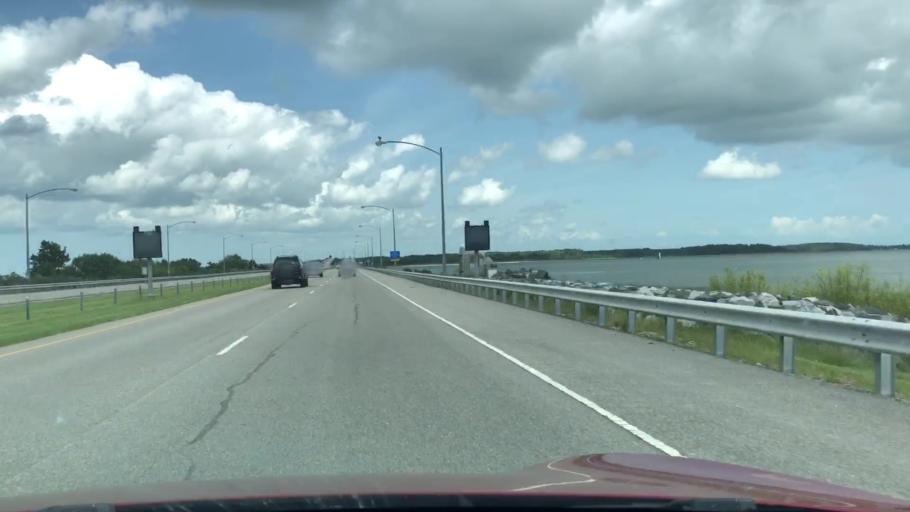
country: US
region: Virginia
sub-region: Northampton County
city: Cape Charles
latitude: 37.1053
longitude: -75.9691
